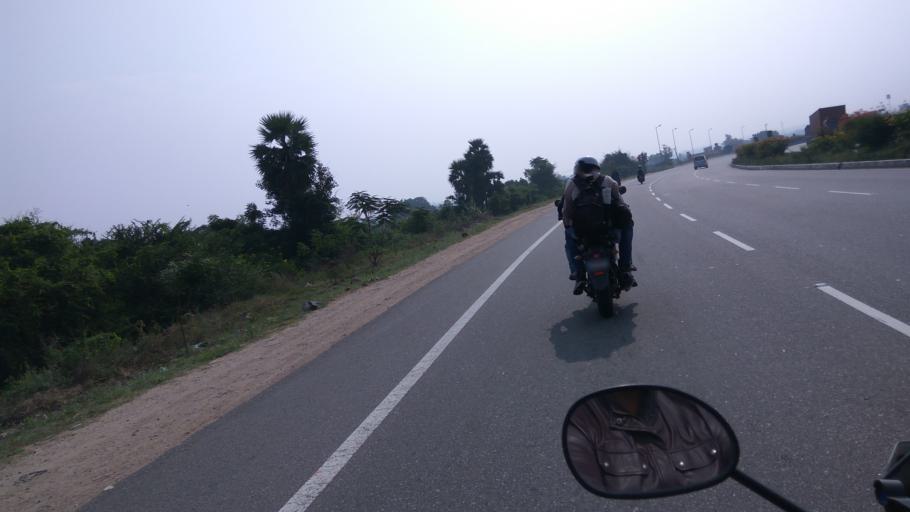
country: IN
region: Tamil Nadu
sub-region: Krishnagiri
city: Krishnagiri
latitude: 12.6054
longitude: 78.1195
